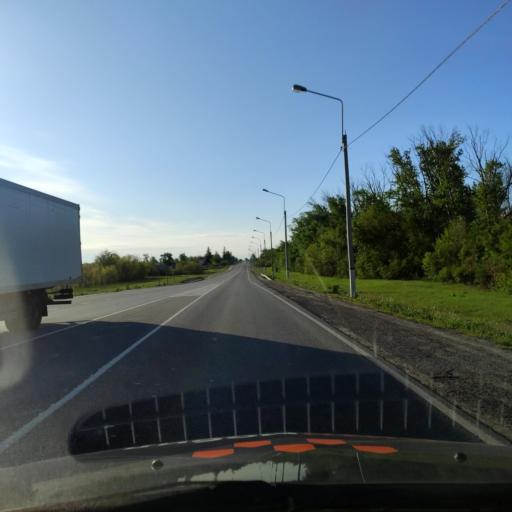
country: RU
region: Lipetsk
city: Yelets
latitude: 52.5603
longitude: 38.6885
